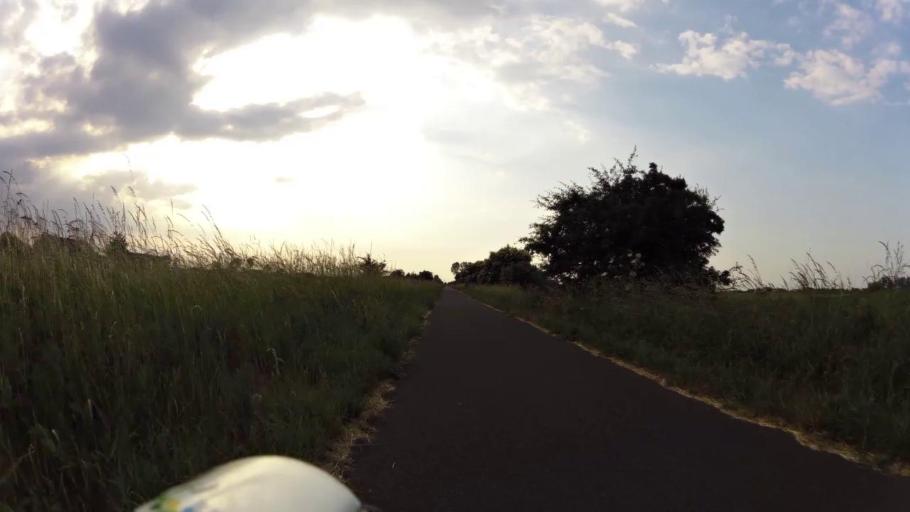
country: PL
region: Kujawsko-Pomorskie
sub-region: Powiat torunski
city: Lubianka
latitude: 53.1666
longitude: 18.4294
